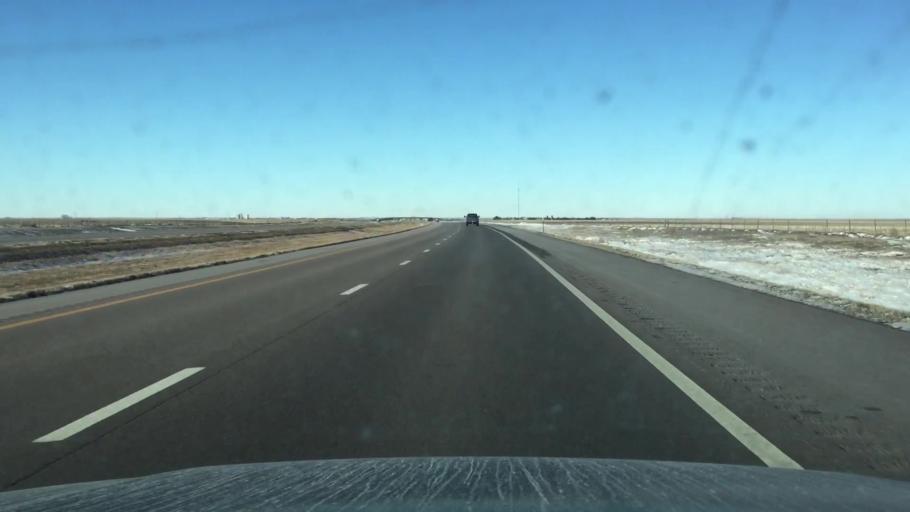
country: US
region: Kansas
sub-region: Logan County
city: Oakley
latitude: 39.2241
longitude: -100.8971
